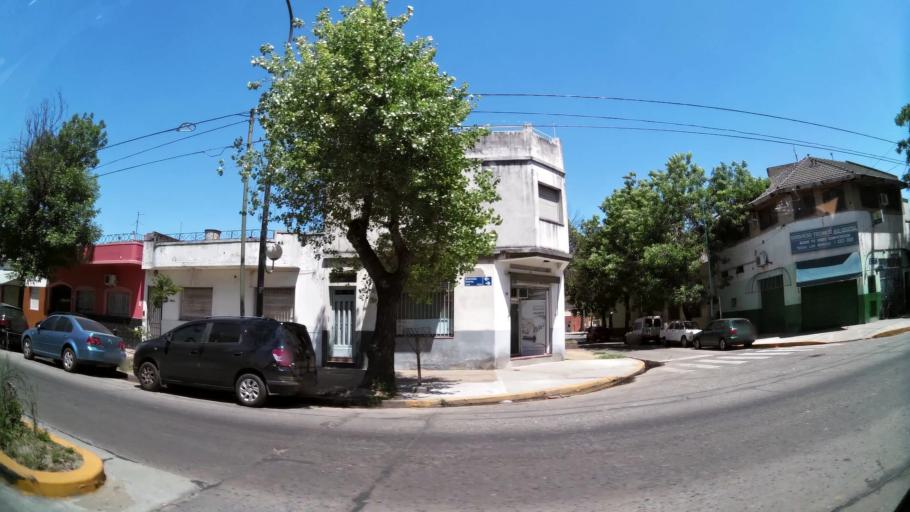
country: AR
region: Buenos Aires
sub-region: Partido de Avellaneda
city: Avellaneda
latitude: -34.6514
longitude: -58.3933
